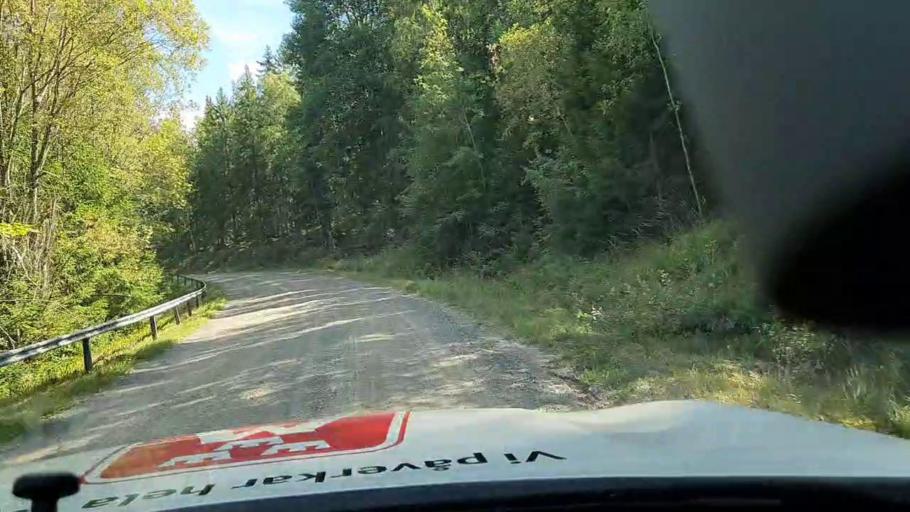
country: SE
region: Soedermanland
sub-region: Strangnas Kommun
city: Akers Styckebruk
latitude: 59.2092
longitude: 16.9121
